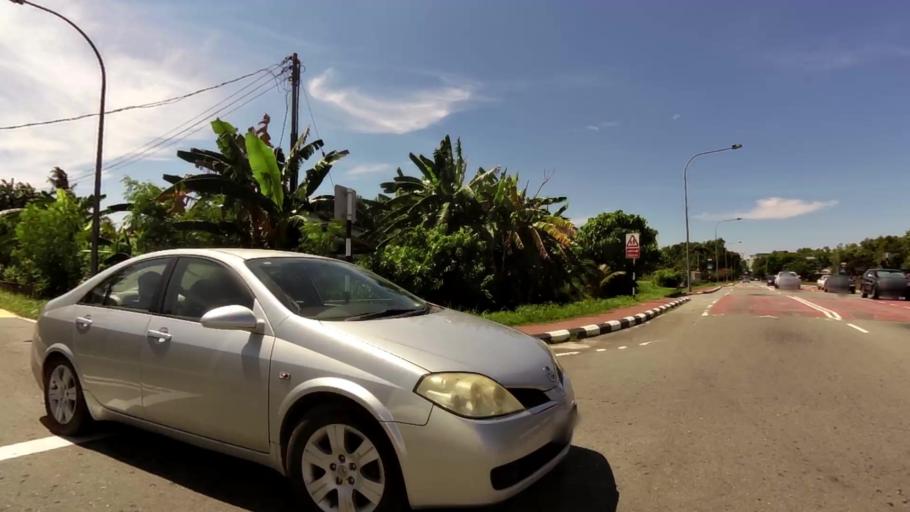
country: BN
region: Brunei and Muara
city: Bandar Seri Begawan
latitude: 4.9402
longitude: 114.9439
